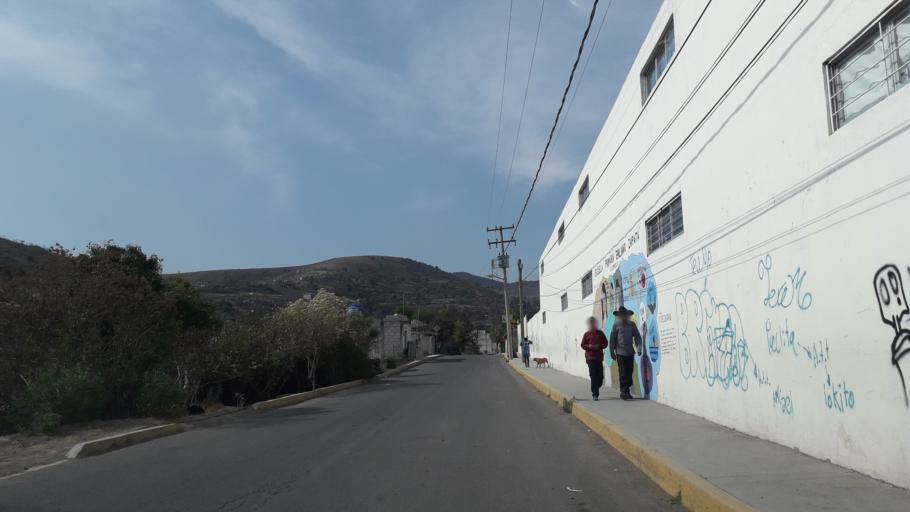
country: MX
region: Puebla
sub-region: Puebla
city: San Andres Azumiatla
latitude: 18.8985
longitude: -98.2564
